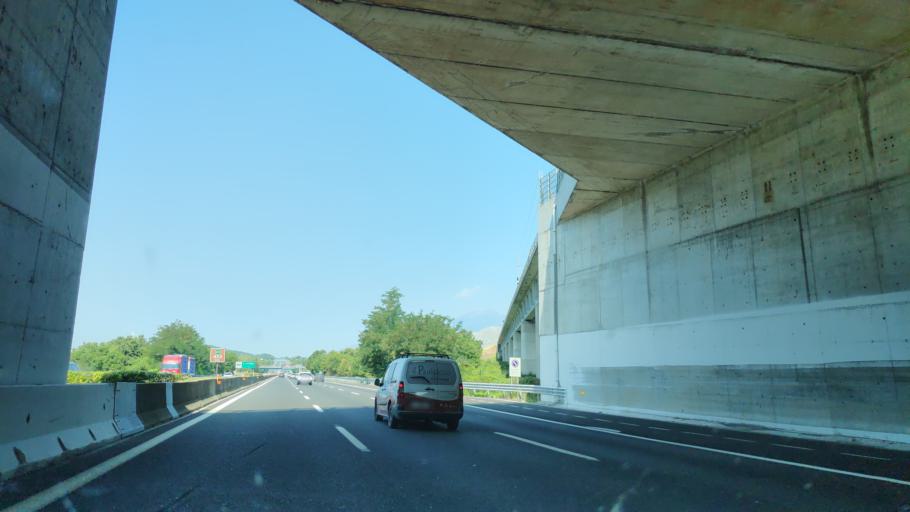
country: IT
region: Campania
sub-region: Provincia di Caserta
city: Bivio Mortola
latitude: 41.4239
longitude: 13.9208
